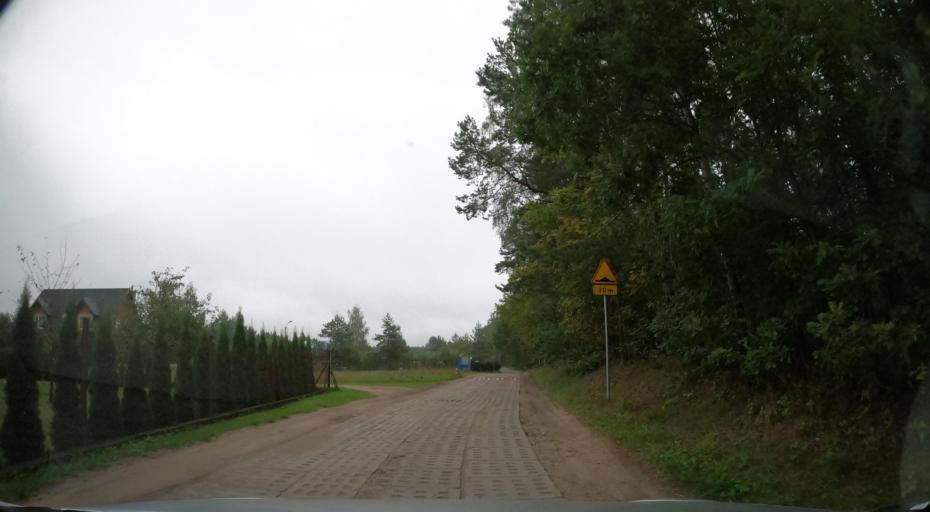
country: PL
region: Pomeranian Voivodeship
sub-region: Powiat kartuski
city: Chwaszczyno
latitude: 54.4217
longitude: 18.4175
